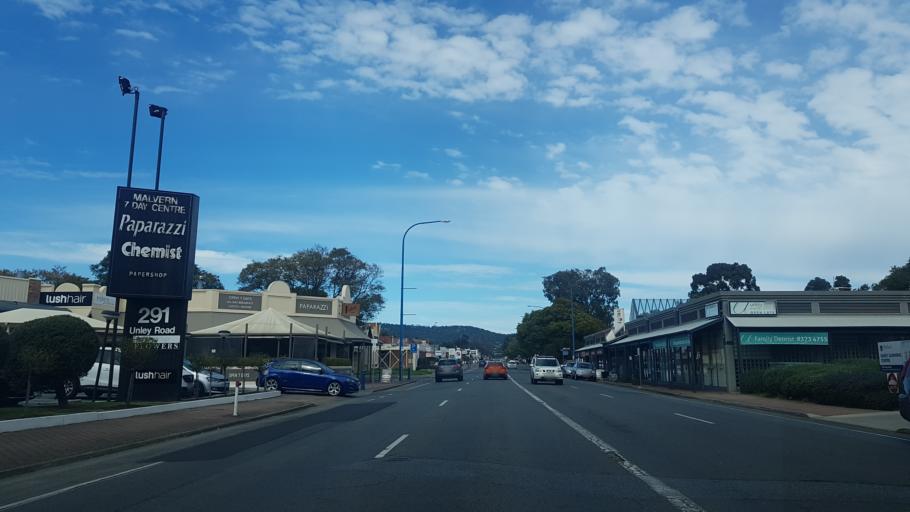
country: AU
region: South Australia
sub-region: Unley
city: Unley Park
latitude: -34.9592
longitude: 138.6082
